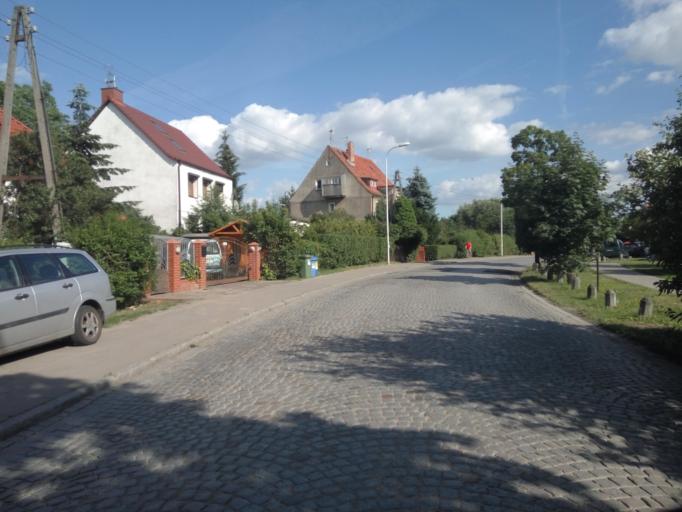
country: PL
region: Lower Silesian Voivodeship
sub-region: Powiat trzebnicki
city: Psary
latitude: 51.1470
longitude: 16.9486
